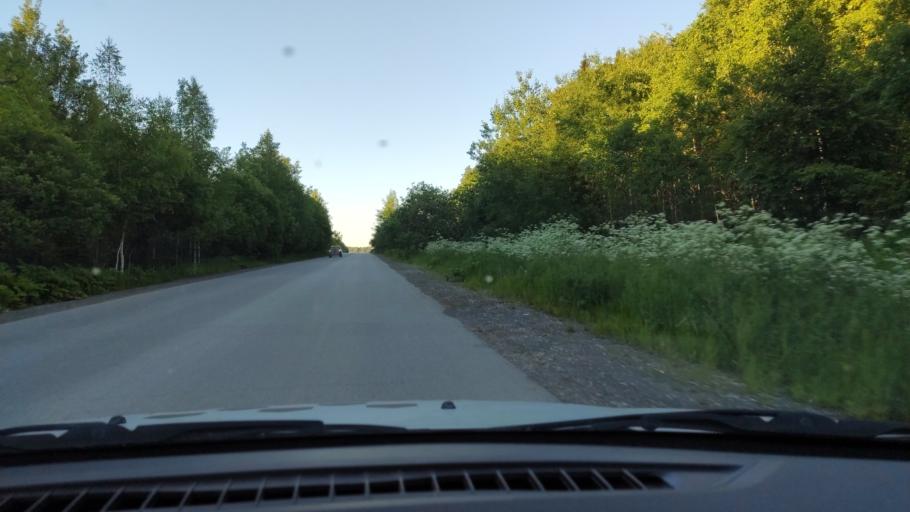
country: RU
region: Perm
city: Ferma
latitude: 57.9861
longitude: 56.3677
